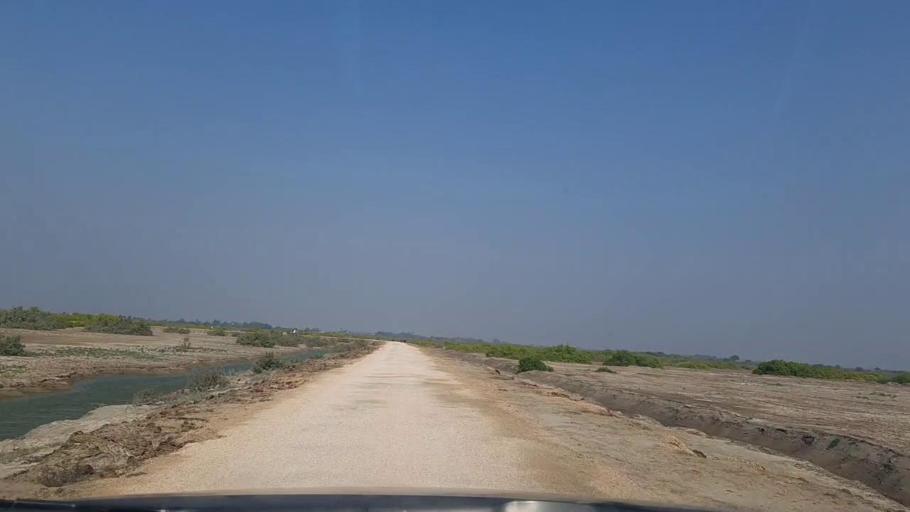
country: PK
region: Sindh
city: Mirpur Sakro
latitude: 24.5771
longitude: 67.7576
